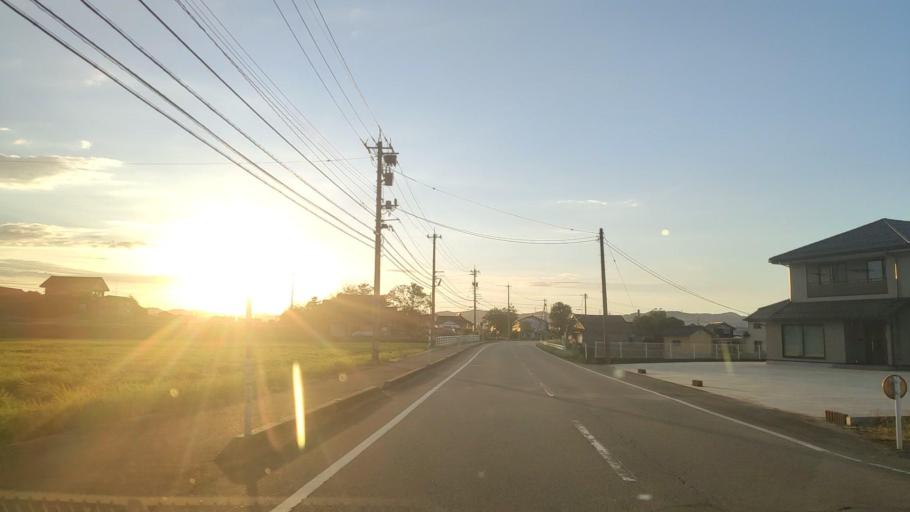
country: JP
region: Toyama
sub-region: Oyabe Shi
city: Oyabe
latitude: 36.6301
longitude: 136.8738
